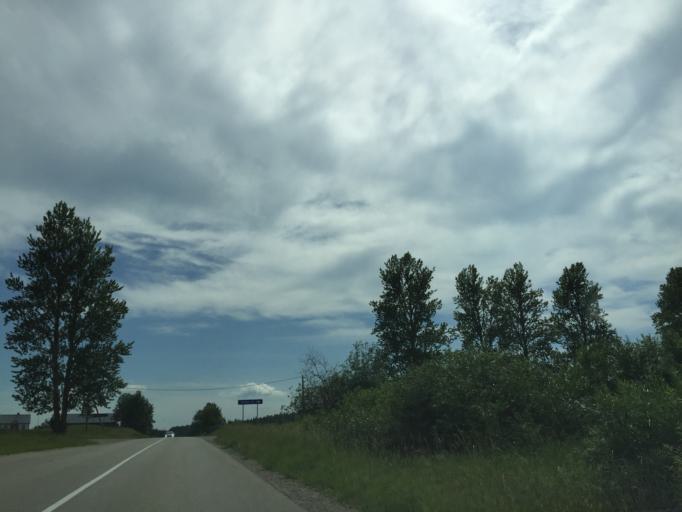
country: LV
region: Tukuma Rajons
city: Tukums
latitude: 57.0315
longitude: 23.2510
